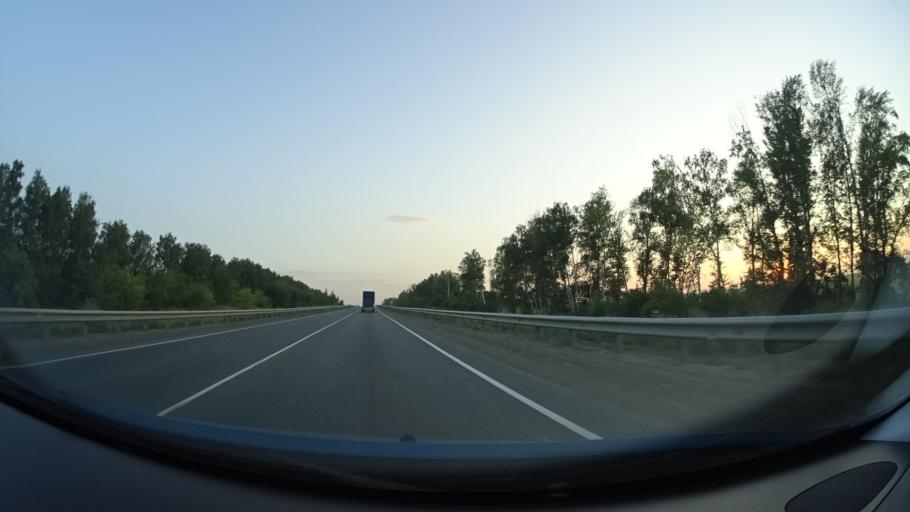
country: RU
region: Samara
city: Sukhodol
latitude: 53.8426
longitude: 51.1177
